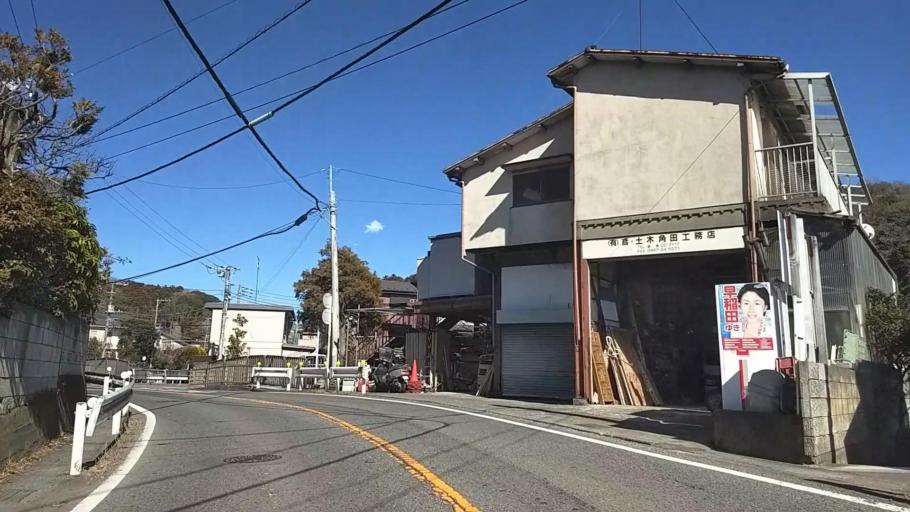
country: JP
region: Kanagawa
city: Zushi
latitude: 35.3202
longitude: 139.5797
